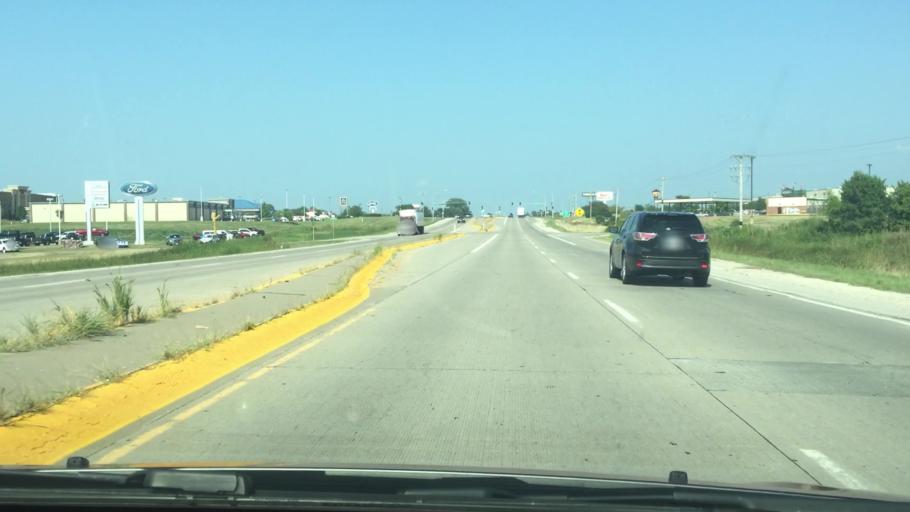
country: US
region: Iowa
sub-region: Muscatine County
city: Muscatine
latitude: 41.4573
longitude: -91.0216
